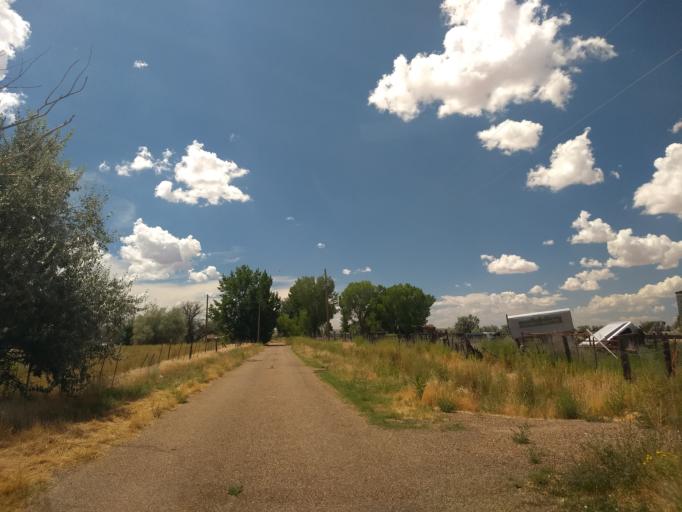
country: US
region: Arizona
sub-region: Coconino County
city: Fredonia
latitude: 36.9404
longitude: -112.5308
